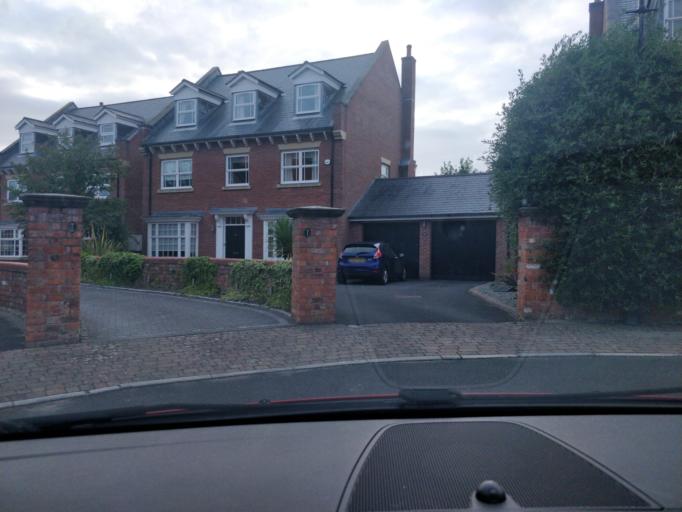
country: GB
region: England
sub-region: Sefton
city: Southport
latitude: 53.6405
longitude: -3.0217
